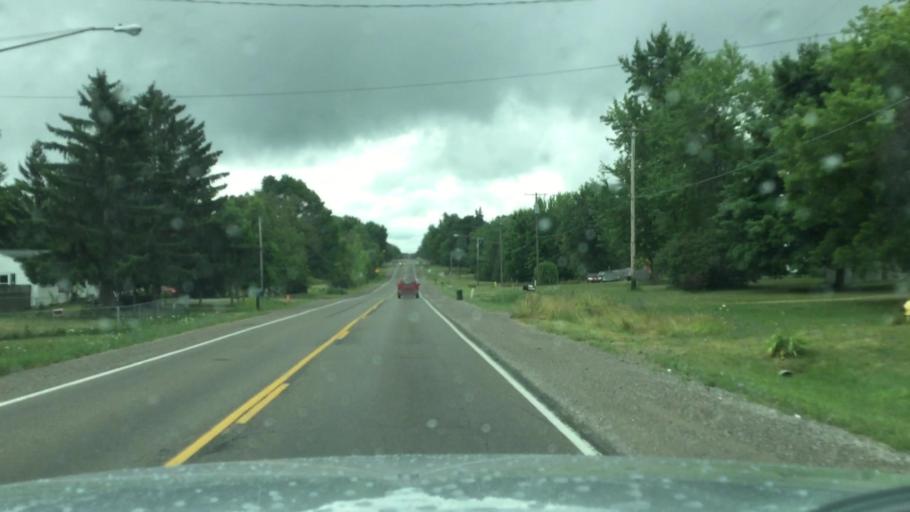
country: US
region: Michigan
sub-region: Genesee County
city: Flushing
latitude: 43.0668
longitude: -83.7731
